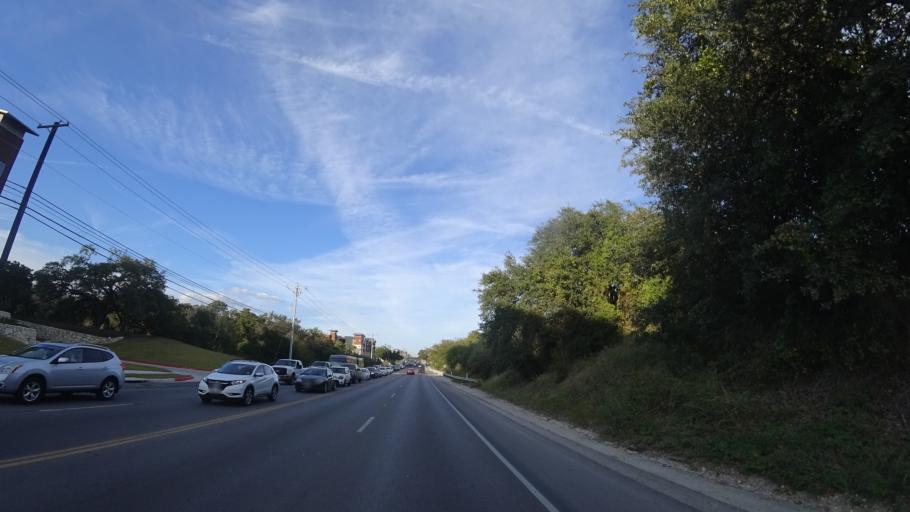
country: US
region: Texas
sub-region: Travis County
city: Austin
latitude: 30.2094
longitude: -97.7724
